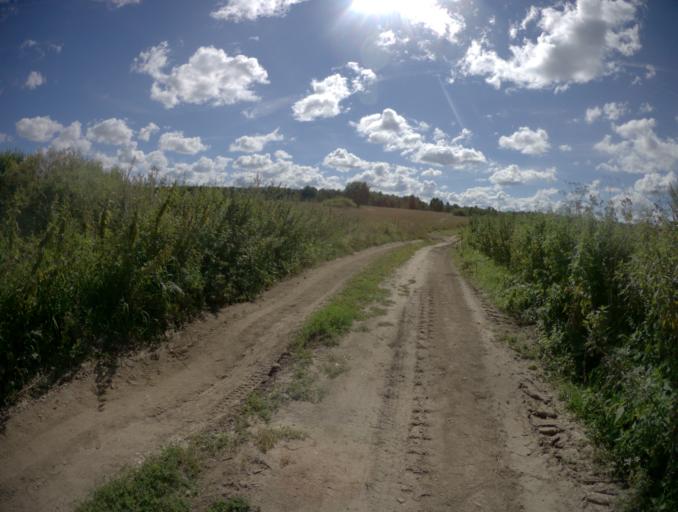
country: RU
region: Vladimir
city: Nikologory
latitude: 56.0081
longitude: 41.8864
